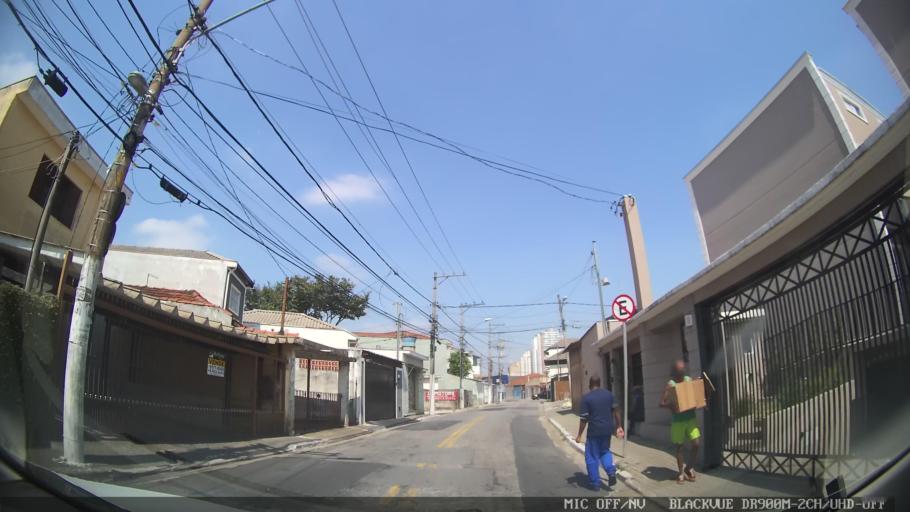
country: BR
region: Sao Paulo
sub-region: Sao Paulo
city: Sao Paulo
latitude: -23.4936
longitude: -46.6411
